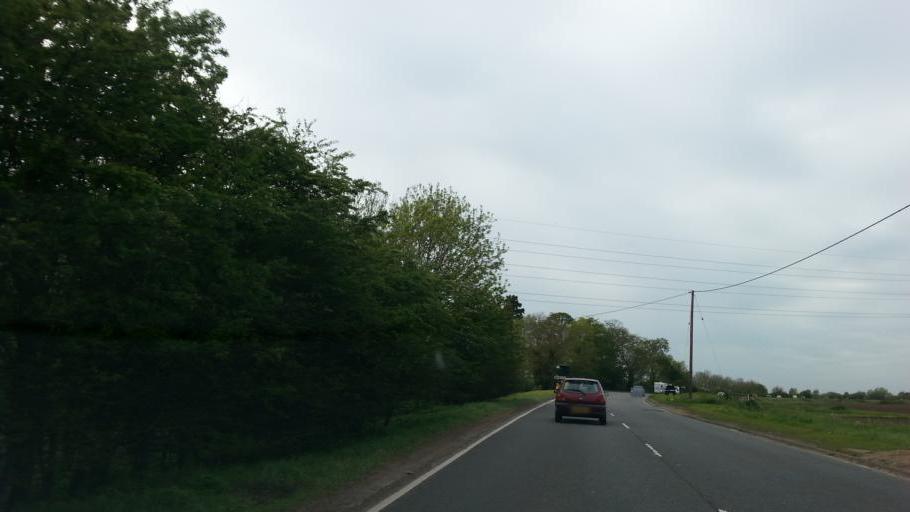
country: GB
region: England
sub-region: Cambridgeshire
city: March
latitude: 52.5738
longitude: 0.0571
